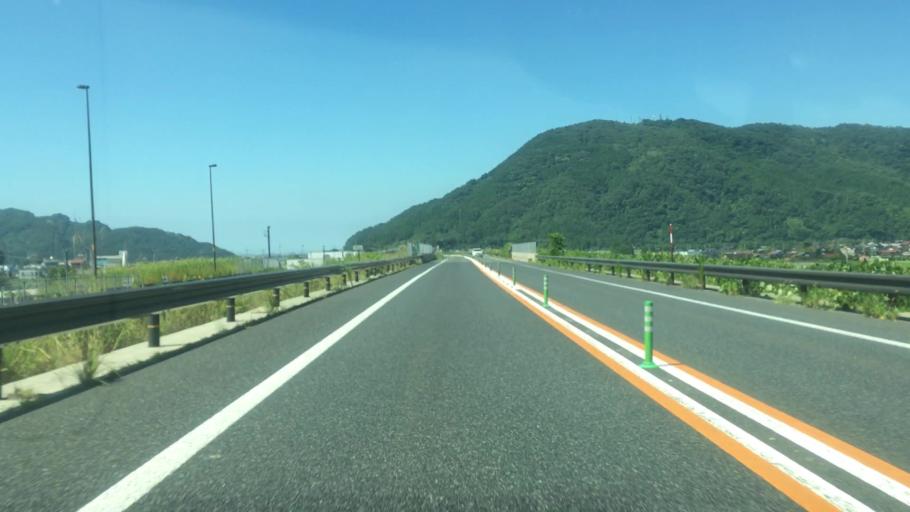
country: JP
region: Tottori
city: Tottori
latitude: 35.3936
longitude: 134.2038
